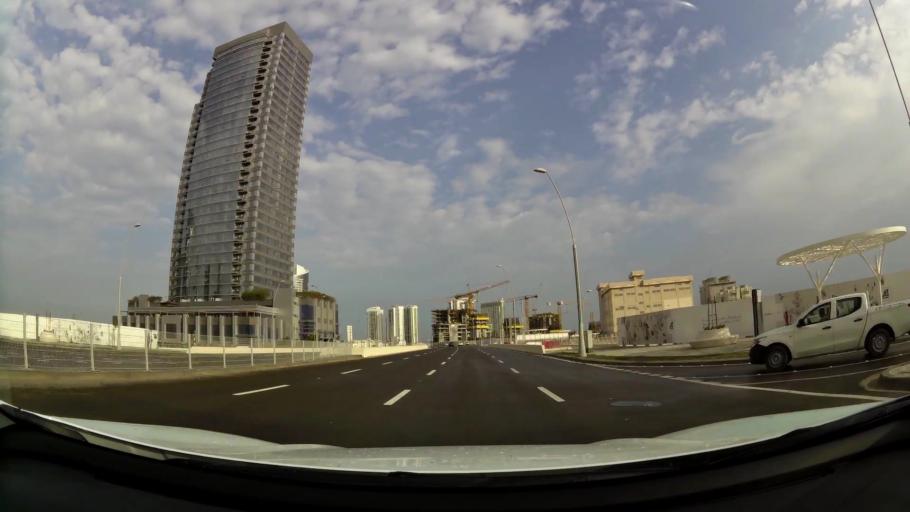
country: AE
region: Abu Dhabi
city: Abu Dhabi
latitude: 24.5007
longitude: 54.4102
